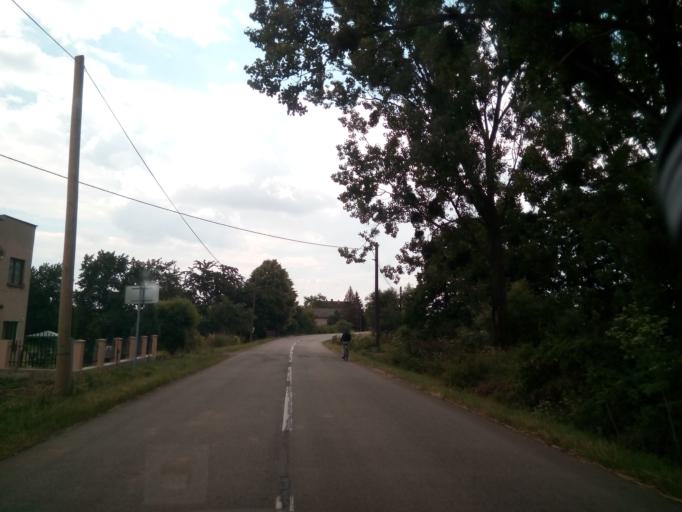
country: SK
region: Kosicky
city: Secovce
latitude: 48.5889
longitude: 21.5656
